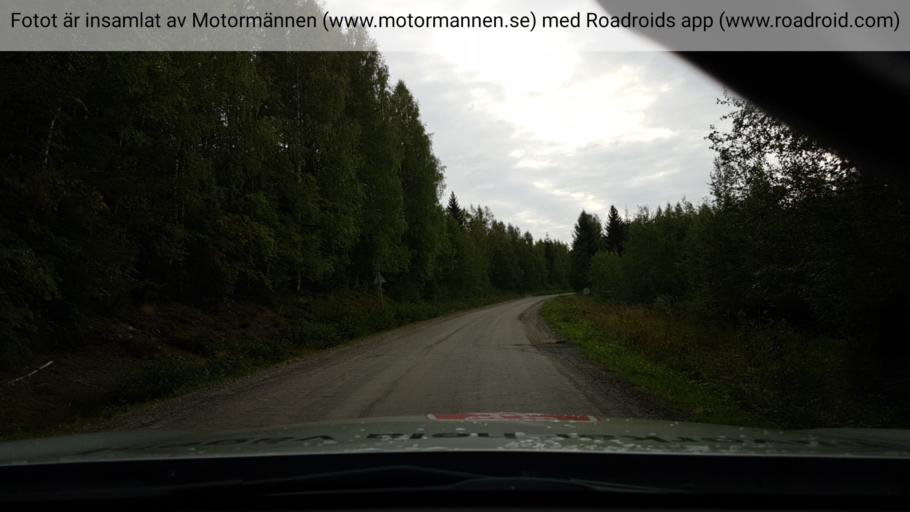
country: SE
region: Vaesterbotten
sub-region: Vannas Kommun
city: Vannasby
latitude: 64.0909
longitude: 20.0311
